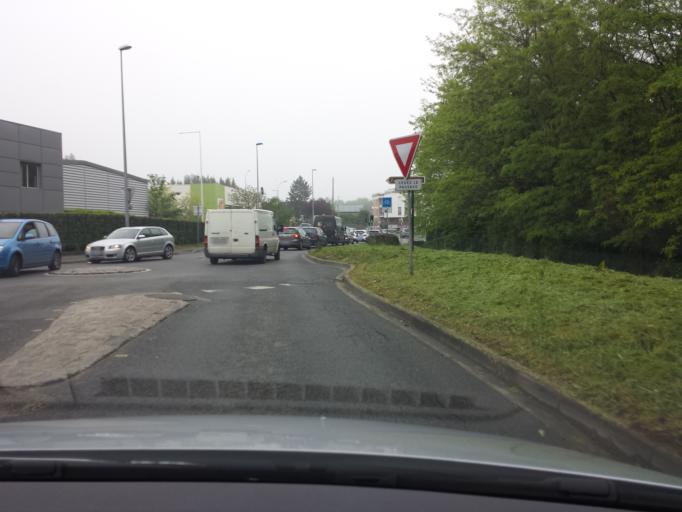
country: FR
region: Ile-de-France
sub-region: Departement de l'Essonne
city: Verrieres-le-Buisson
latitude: 48.7445
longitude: 2.2819
